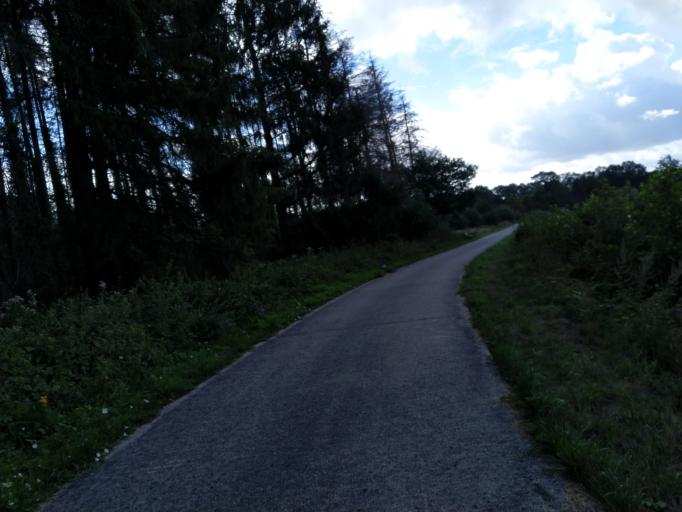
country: BE
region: Wallonia
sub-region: Province du Hainaut
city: Merbes-le-Chateau
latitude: 50.3261
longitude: 4.2161
